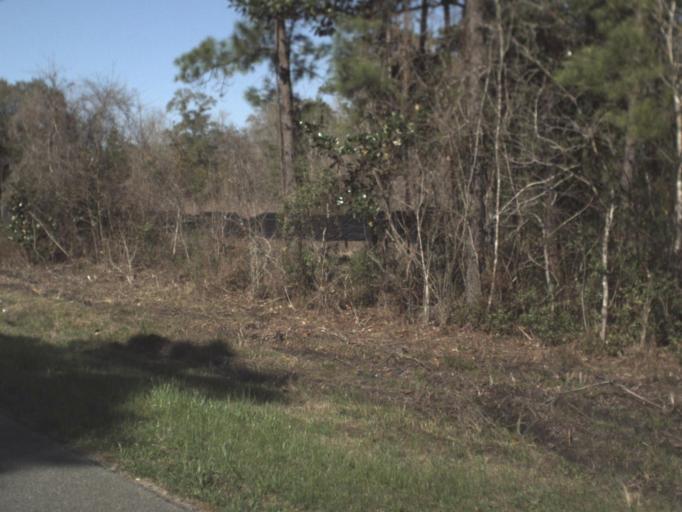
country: US
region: Florida
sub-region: Jackson County
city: Marianna
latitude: 30.6941
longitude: -85.1808
